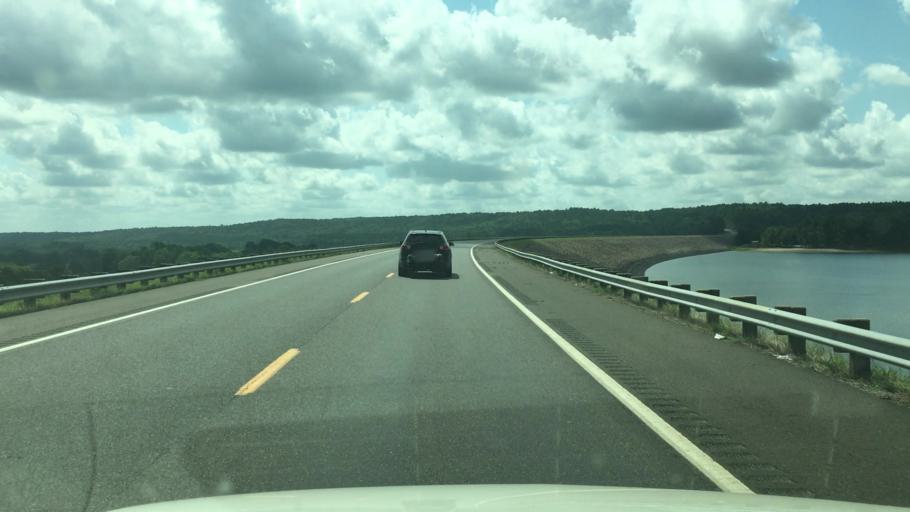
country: US
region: Arkansas
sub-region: Clark County
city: Arkadelphia
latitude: 34.2446
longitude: -93.1078
